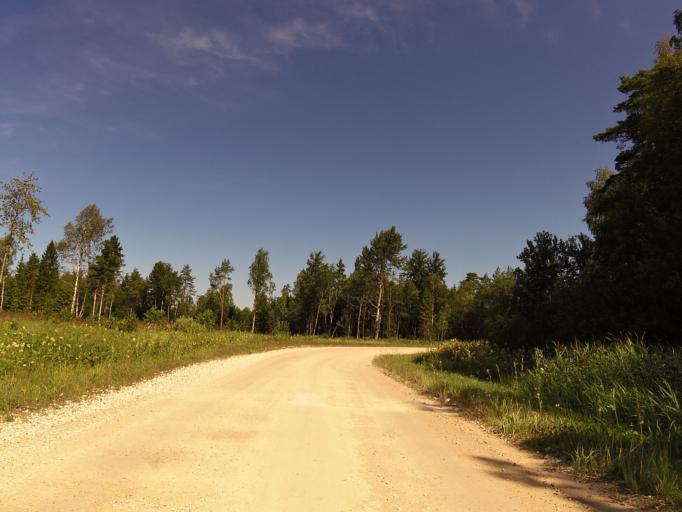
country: EE
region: Hiiumaa
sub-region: Kaerdla linn
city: Kardla
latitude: 58.9277
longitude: 22.3697
